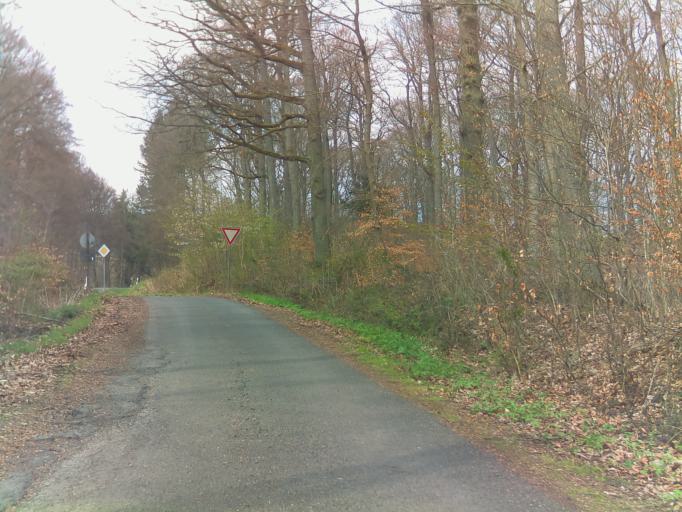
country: DE
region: Rheinland-Pfalz
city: Heinzenberg
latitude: 49.8031
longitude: 7.4759
